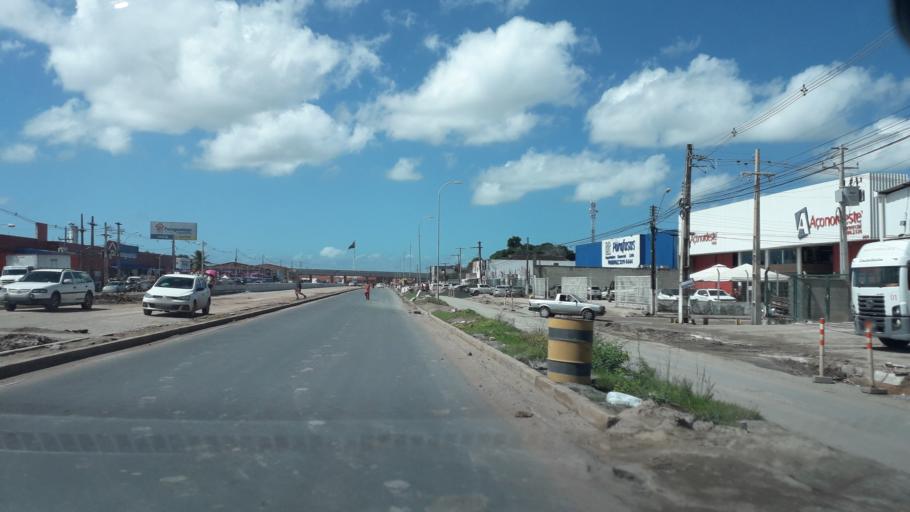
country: BR
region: Alagoas
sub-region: Satuba
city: Satuba
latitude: -9.5658
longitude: -35.7813
